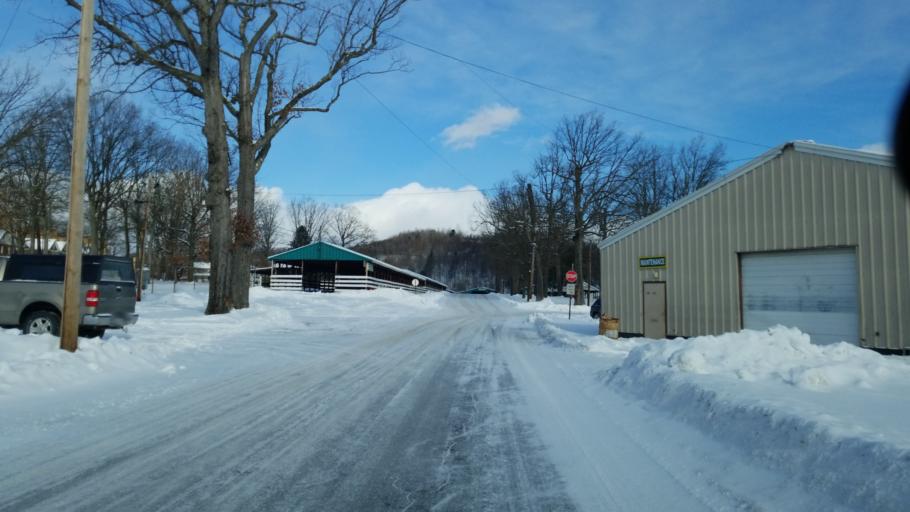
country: US
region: Pennsylvania
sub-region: Clearfield County
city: Clearfield
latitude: 41.0302
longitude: -78.4467
